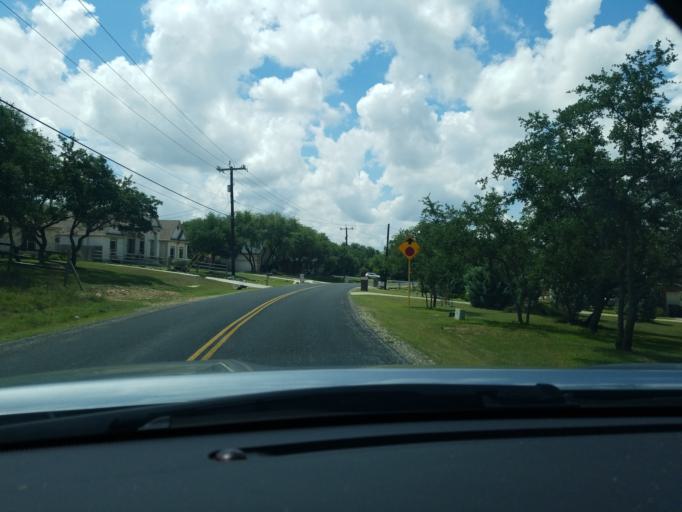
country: US
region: Texas
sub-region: Bexar County
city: Timberwood Park
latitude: 29.6863
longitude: -98.4860
